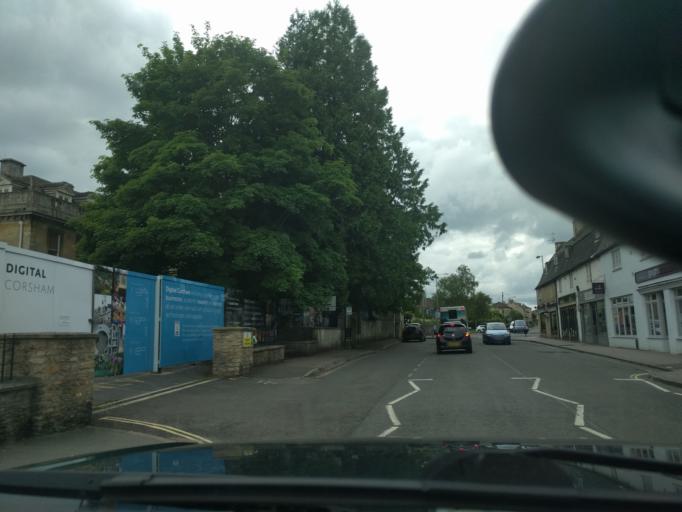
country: GB
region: England
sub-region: Wiltshire
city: Corsham
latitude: 51.4314
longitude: -2.1868
